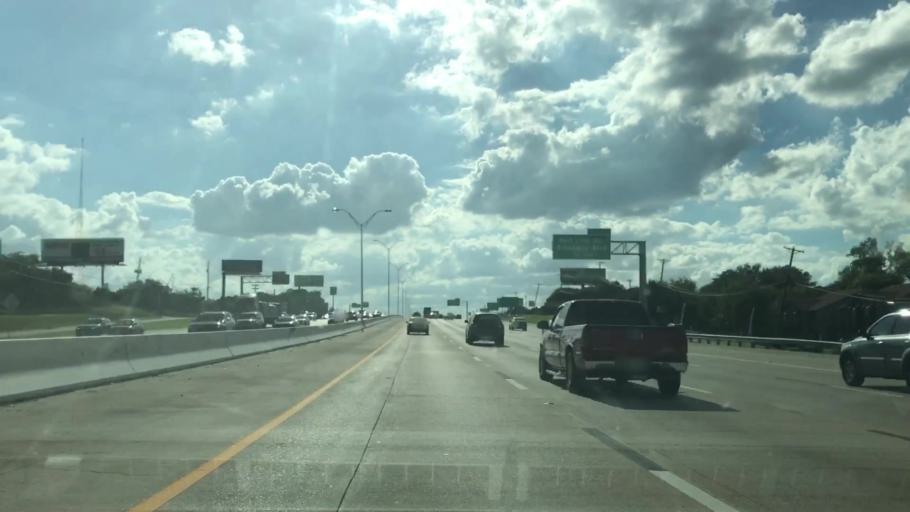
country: US
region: Texas
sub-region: Dallas County
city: Sunnyvale
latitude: 32.8437
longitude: -96.5868
